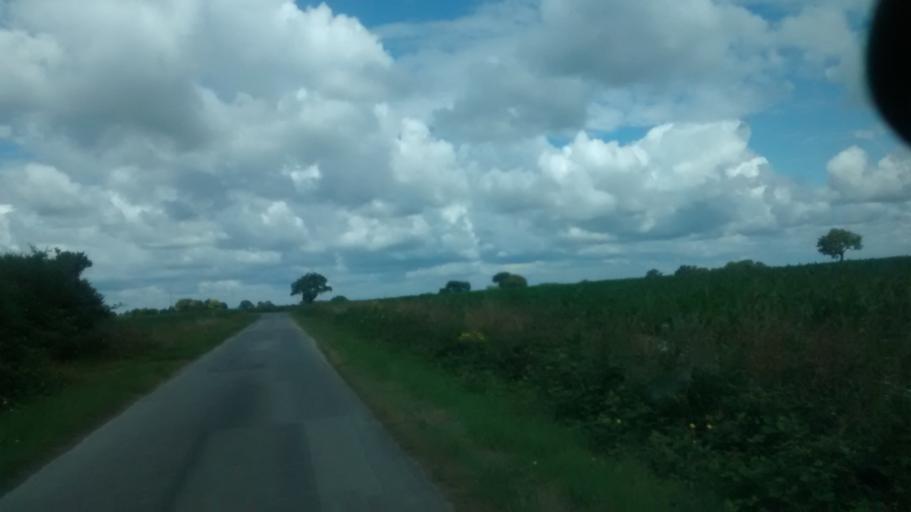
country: FR
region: Brittany
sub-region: Departement d'Ille-et-Vilaine
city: Grand-Fougeray
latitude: 47.7786
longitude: -1.7470
